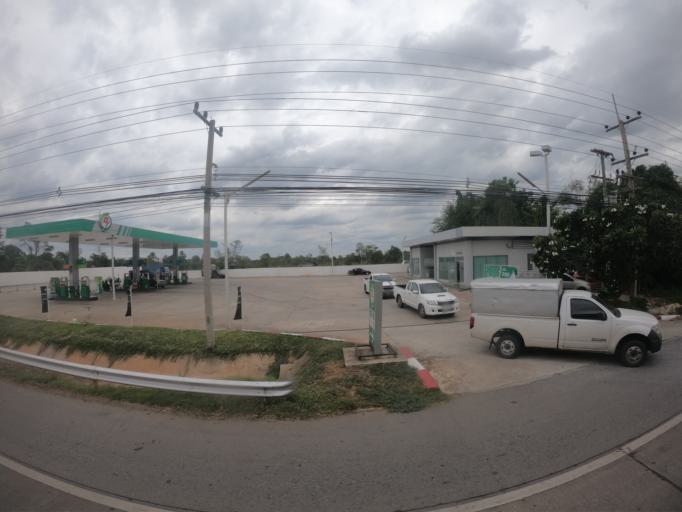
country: TH
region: Nakhon Ratchasima
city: Chok Chai
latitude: 14.7570
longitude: 102.1636
